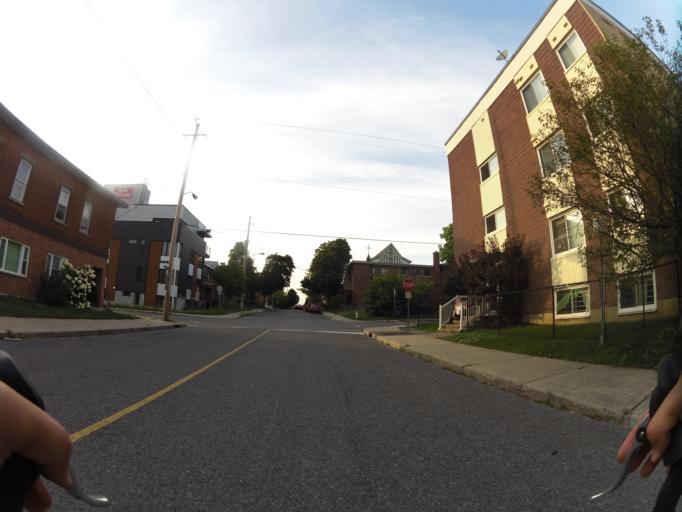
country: CA
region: Ontario
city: Ottawa
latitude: 45.4047
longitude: -75.7062
